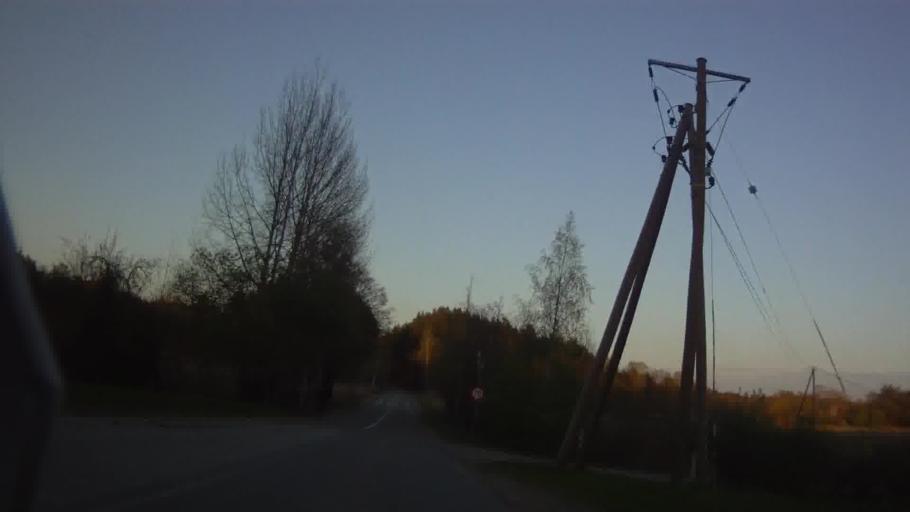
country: LV
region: Riga
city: Jaunciems
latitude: 57.0122
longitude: 24.2253
